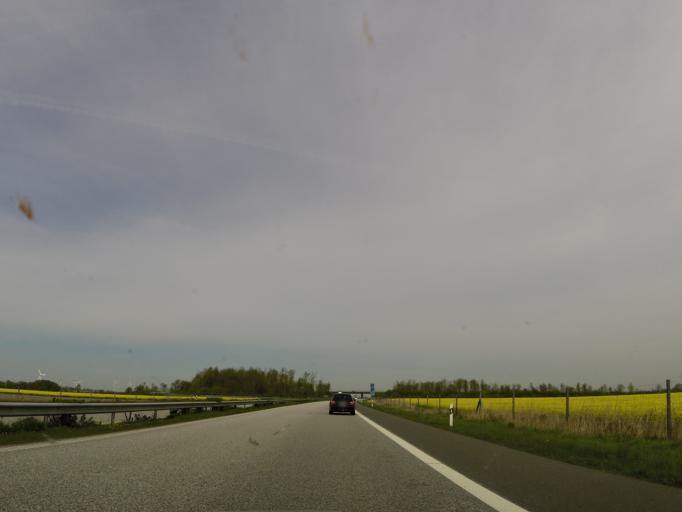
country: DE
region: Schleswig-Holstein
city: Lohe-Rickelshof
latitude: 54.1855
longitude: 9.0494
